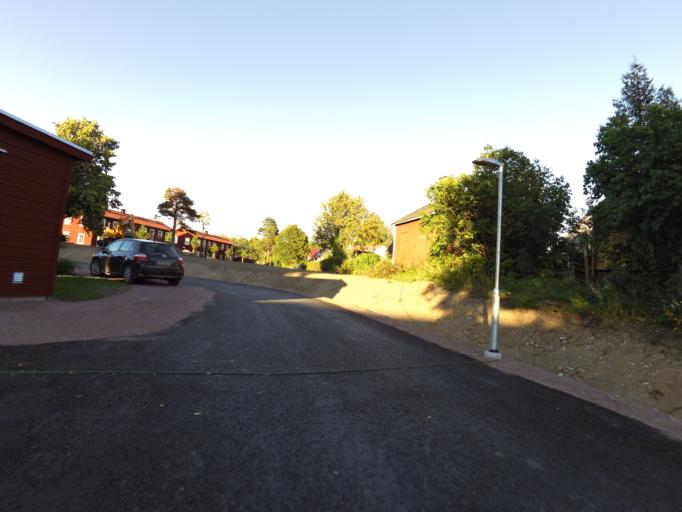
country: SE
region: Gaevleborg
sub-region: Gavle Kommun
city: Gavle
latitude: 60.7126
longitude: 17.1608
